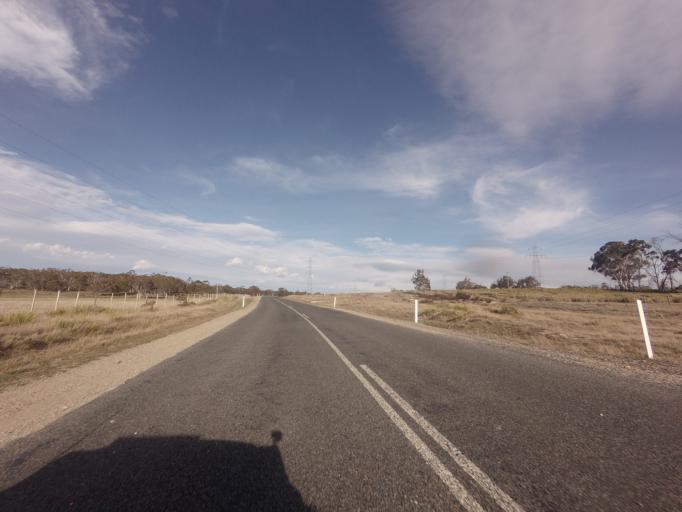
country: AU
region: Tasmania
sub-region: Derwent Valley
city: New Norfolk
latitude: -42.2730
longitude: 146.9437
